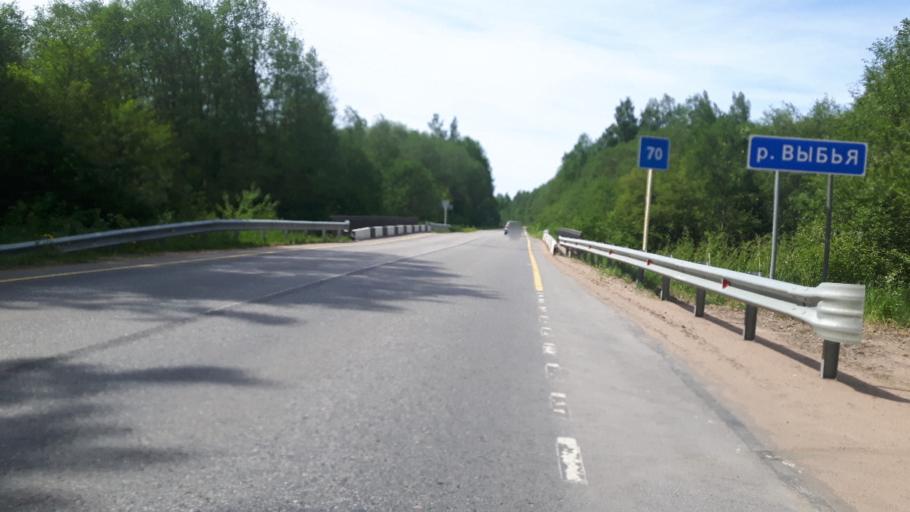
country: RU
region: Leningrad
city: Ust'-Luga
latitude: 59.6466
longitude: 28.2102
